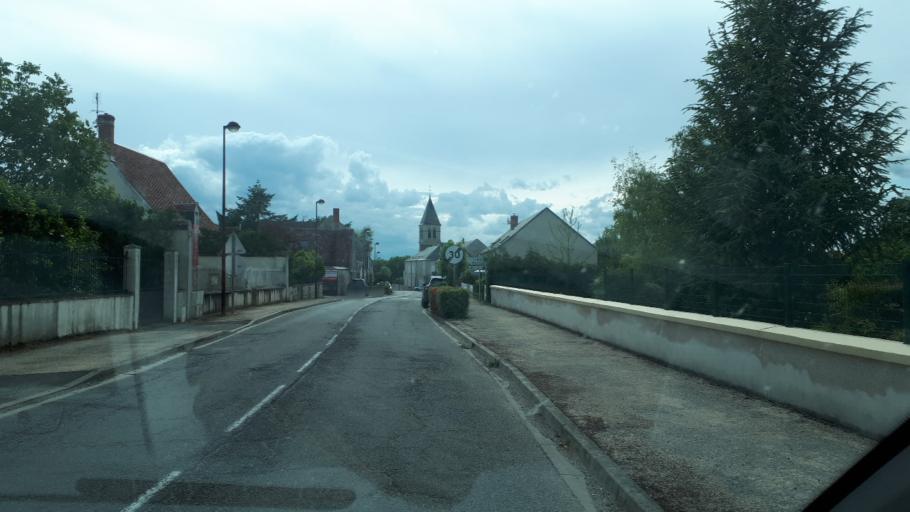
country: FR
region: Centre
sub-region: Departement du Cher
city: Mehun-sur-Yevre
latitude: 47.0813
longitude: 2.2012
